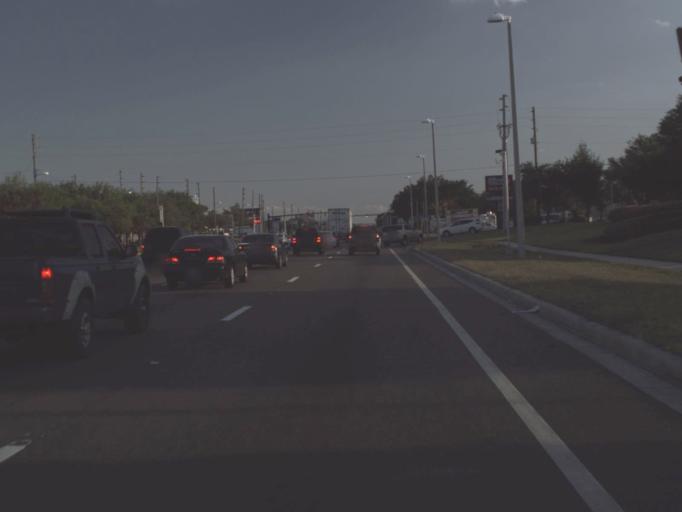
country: US
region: Florida
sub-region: Orange County
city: Southchase
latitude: 28.4004
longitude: -81.4047
